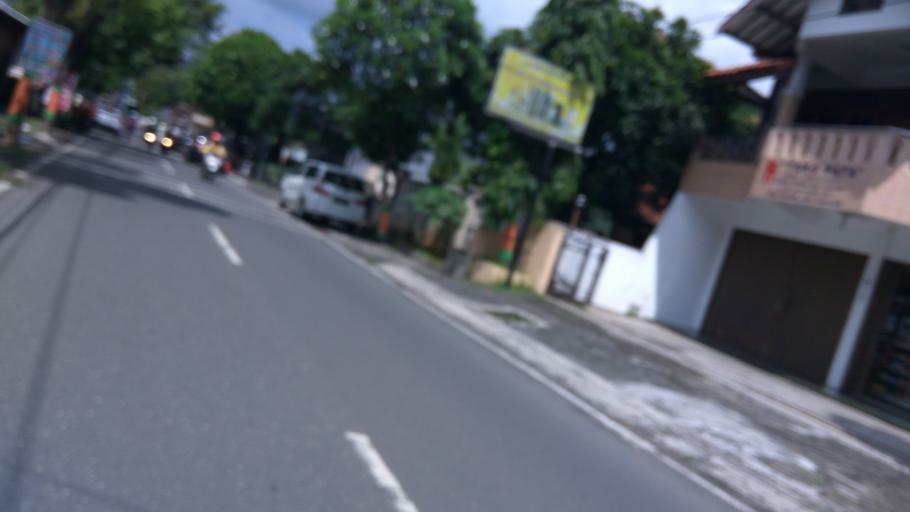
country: ID
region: Central Java
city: Ungaran
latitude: -7.1287
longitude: 110.4072
